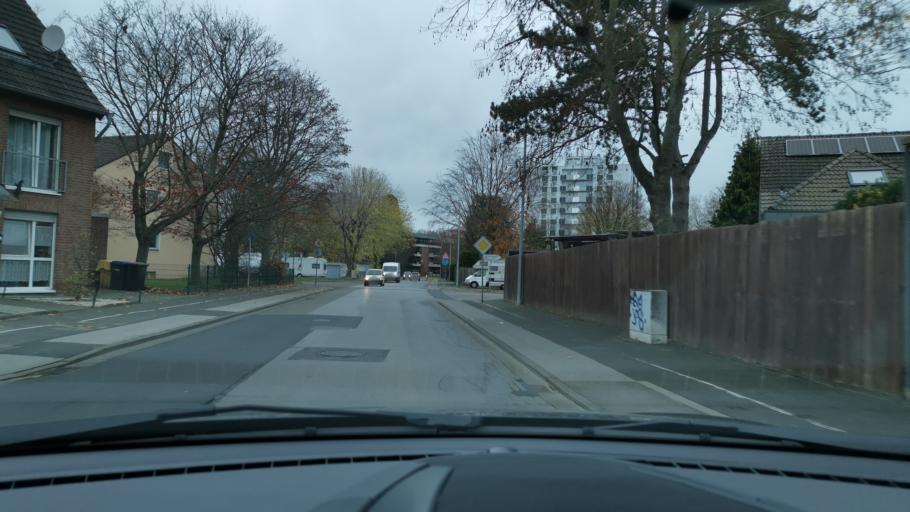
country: DE
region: North Rhine-Westphalia
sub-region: Regierungsbezirk Dusseldorf
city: Grevenbroich
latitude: 51.0767
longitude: 6.6009
